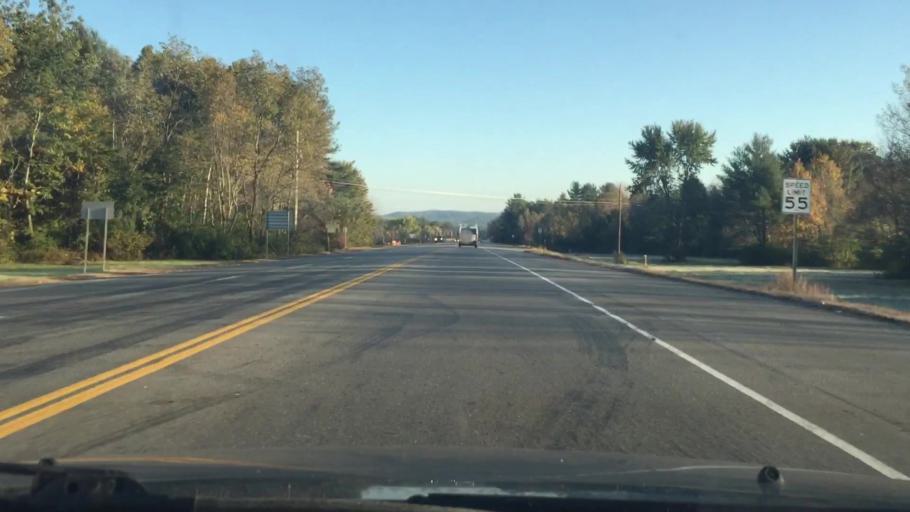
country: US
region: New Hampshire
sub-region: Cheshire County
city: Keene
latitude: 42.9246
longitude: -72.2997
